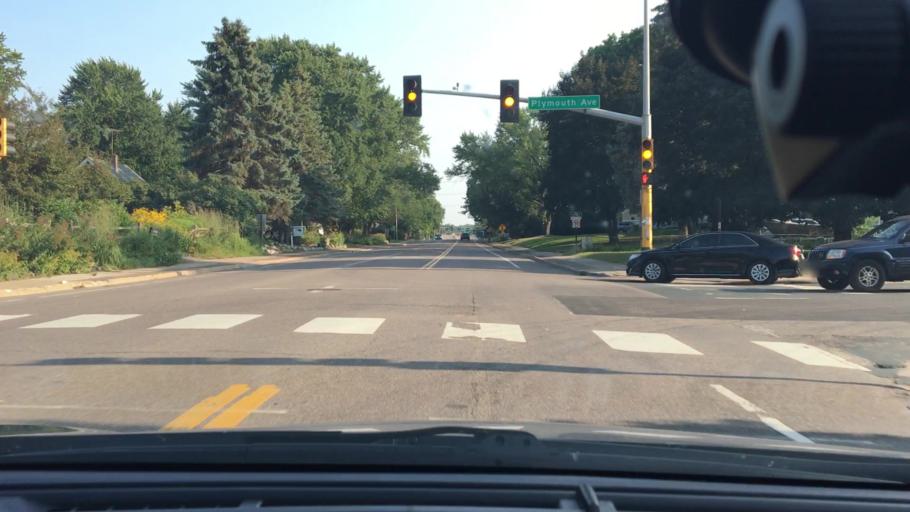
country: US
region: Minnesota
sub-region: Hennepin County
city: Golden Valley
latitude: 44.9929
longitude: -93.3805
